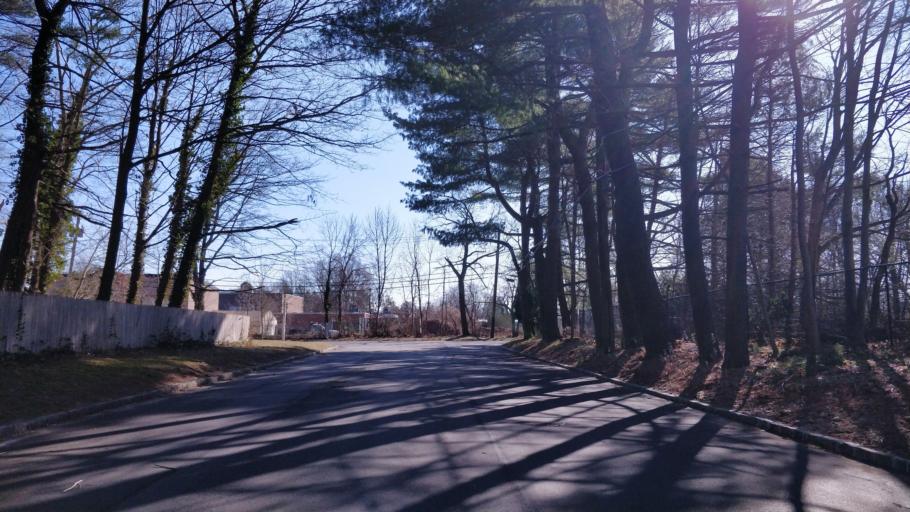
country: US
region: New York
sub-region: Nassau County
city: East Norwich
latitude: 40.8512
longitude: -73.5392
